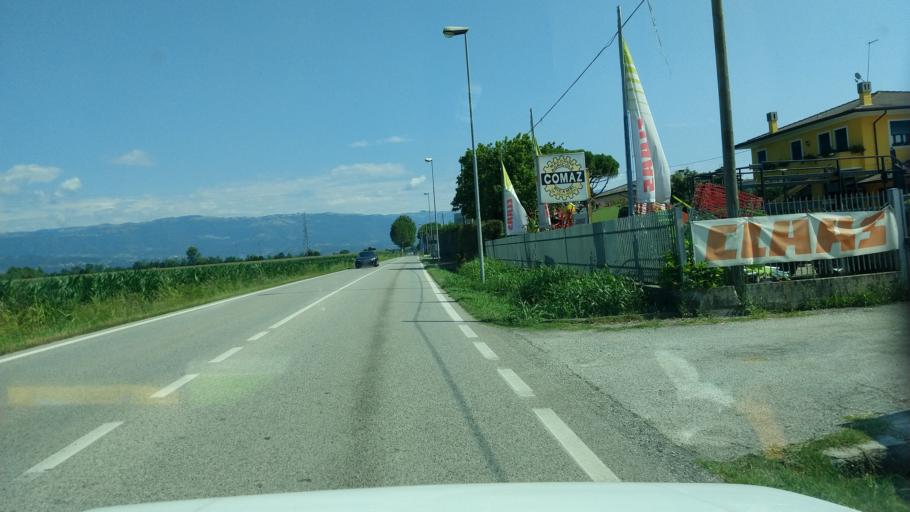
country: IT
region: Veneto
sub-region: Provincia di Vicenza
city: Schiavon
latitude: 45.6786
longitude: 11.6671
